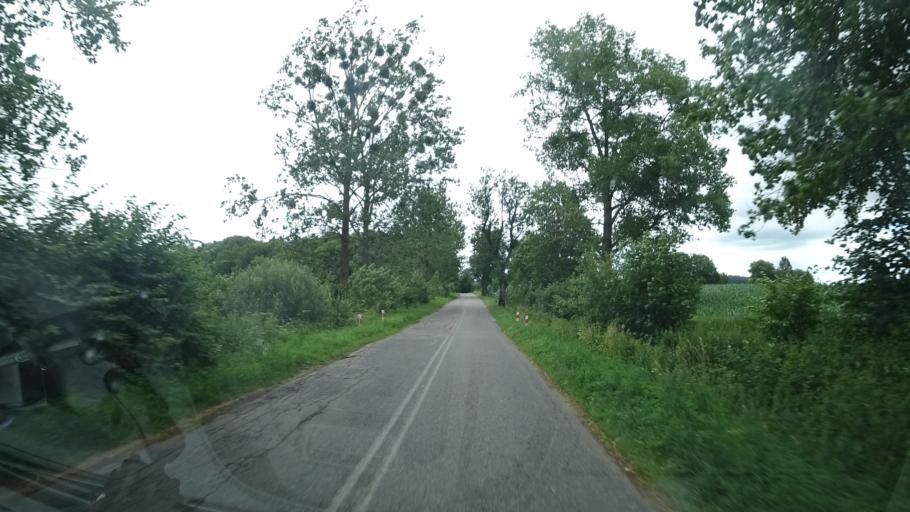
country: PL
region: Warmian-Masurian Voivodeship
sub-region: Powiat olecki
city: Kowale Oleckie
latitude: 54.2893
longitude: 22.5074
